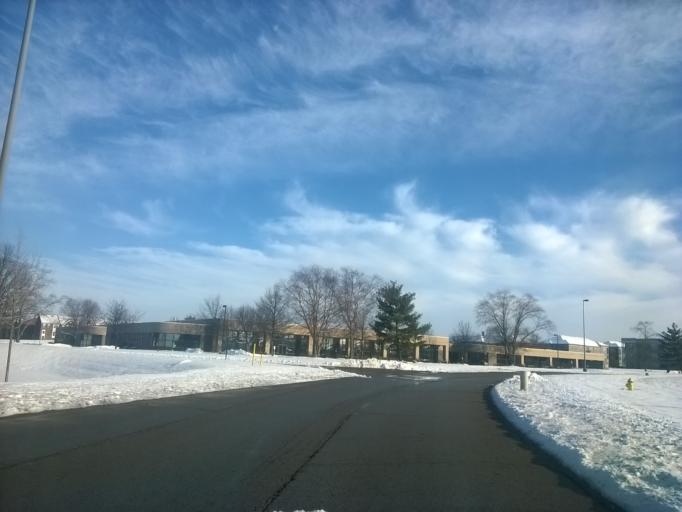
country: US
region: Indiana
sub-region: Hamilton County
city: Carmel
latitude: 39.9604
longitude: -86.1465
